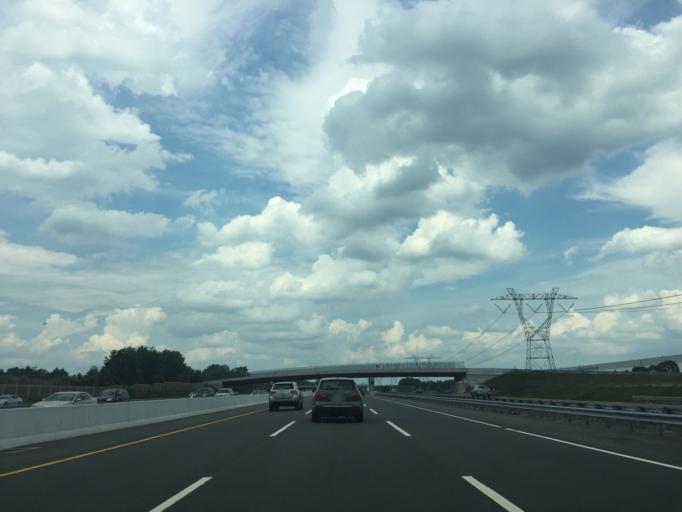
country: US
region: New Jersey
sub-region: Monmouth County
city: Allentown
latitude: 40.2041
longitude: -74.5856
